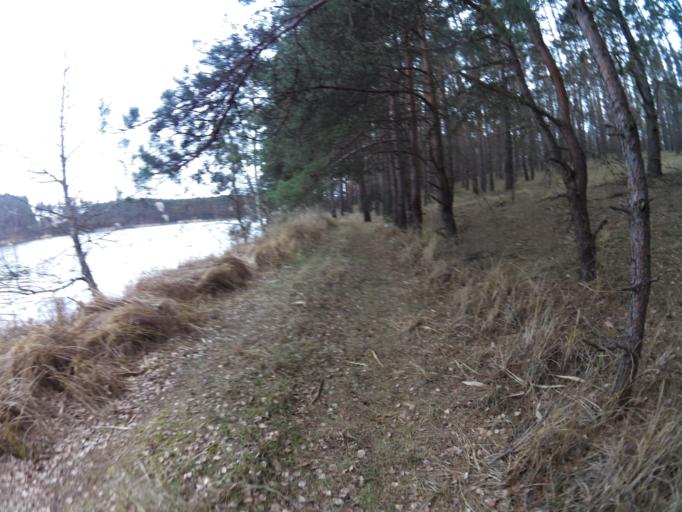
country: PL
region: West Pomeranian Voivodeship
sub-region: Powiat mysliborski
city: Debno
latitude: 52.7615
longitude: 14.8018
